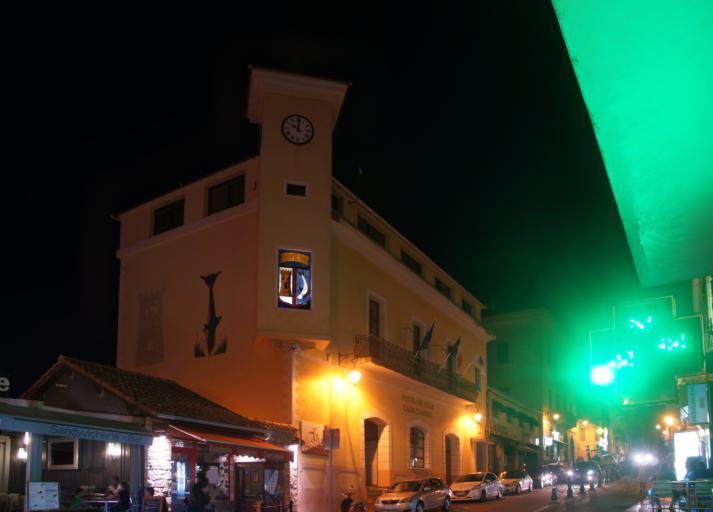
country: FR
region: Corsica
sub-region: Departement de la Corse-du-Sud
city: Propriano
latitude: 41.6759
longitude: 8.9043
